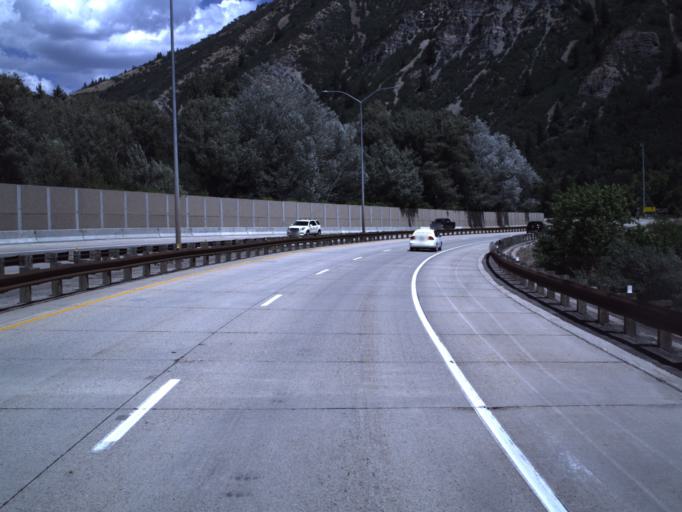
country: US
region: Utah
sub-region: Utah County
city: Orem
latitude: 40.3634
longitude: -111.5598
